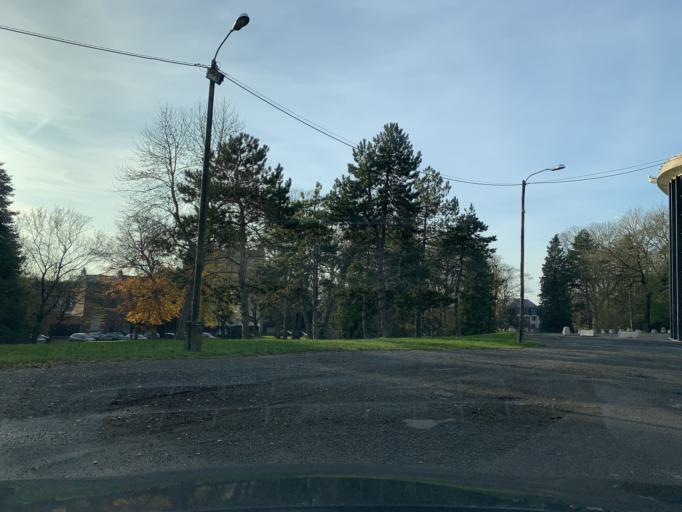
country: FR
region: Nord-Pas-de-Calais
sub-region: Departement du Nord
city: Cambrai
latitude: 50.1694
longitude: 3.2403
